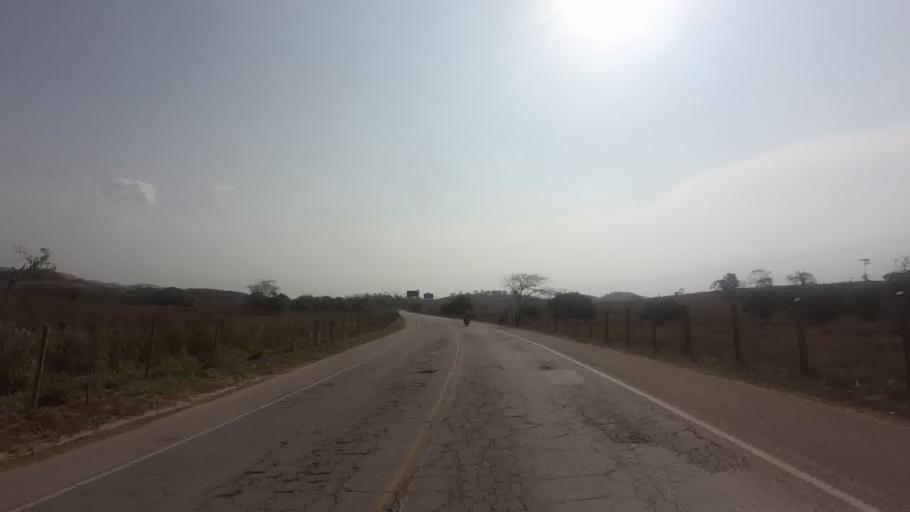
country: BR
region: Rio de Janeiro
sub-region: Bom Jesus Do Itabapoana
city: Bom Jesus do Itabapoana
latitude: -21.1465
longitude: -41.5823
